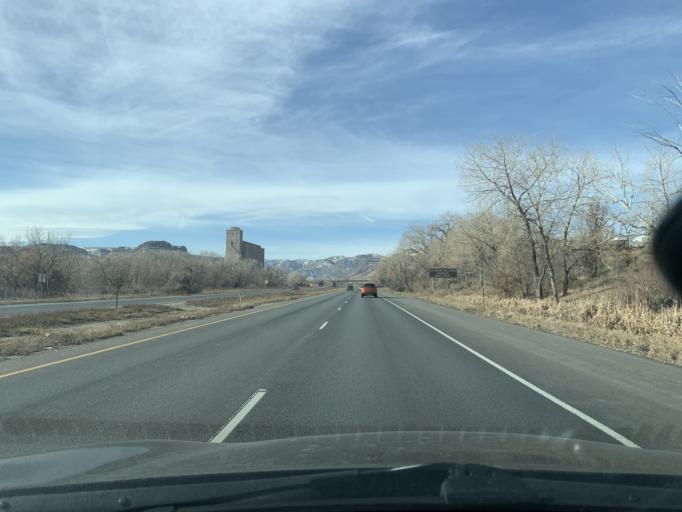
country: US
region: Colorado
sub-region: Jefferson County
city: Applewood
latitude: 39.7743
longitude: -105.1647
